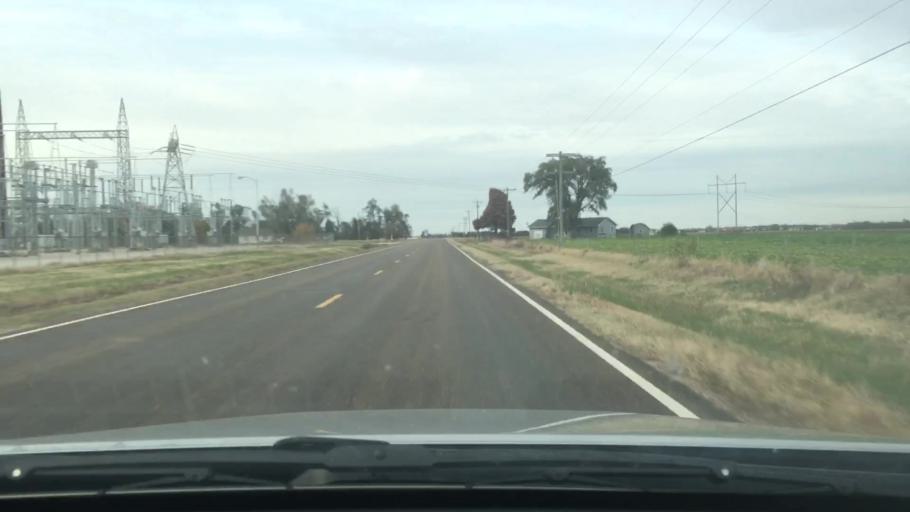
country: US
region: Kansas
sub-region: Sedgwick County
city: Colwich
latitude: 37.7921
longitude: -97.5182
